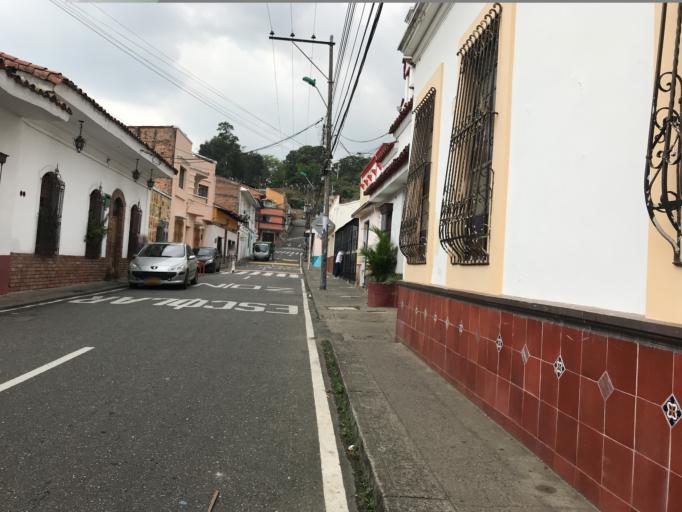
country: CO
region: Valle del Cauca
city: Cali
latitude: 3.4481
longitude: -76.5391
